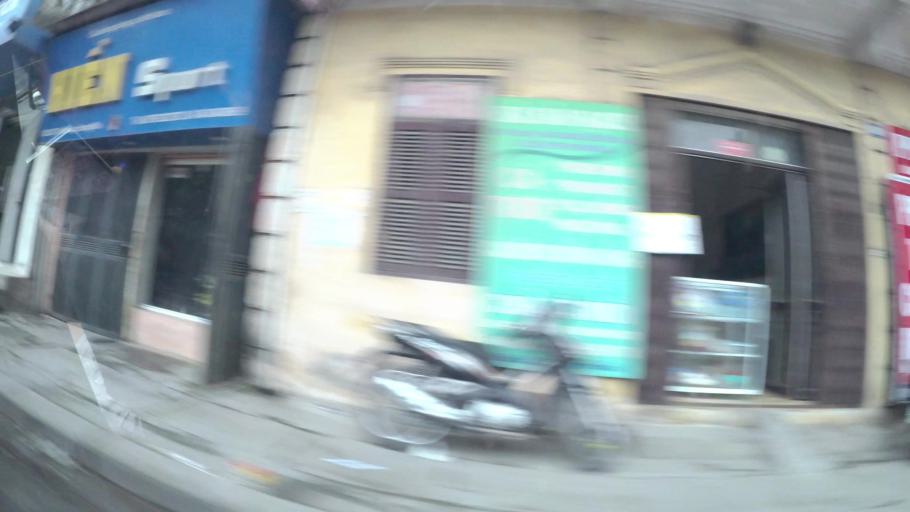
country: VN
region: Ha Noi
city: Hai BaTrung
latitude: 20.9979
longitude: 105.8797
